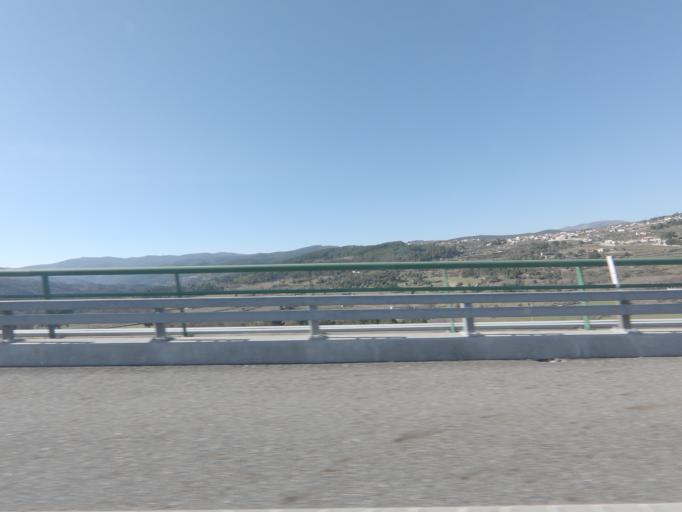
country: PT
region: Vila Real
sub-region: Boticas
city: Boticas
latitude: 41.6393
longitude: -7.5922
